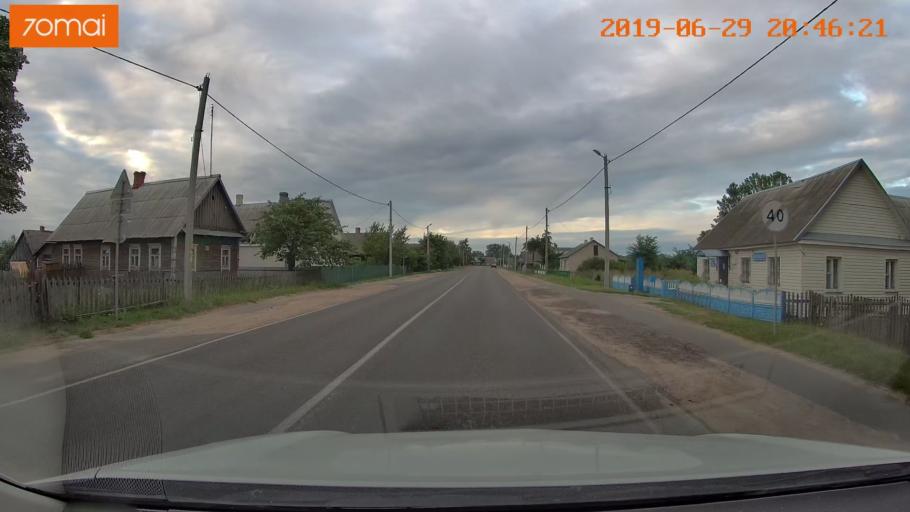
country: BY
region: Brest
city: Hantsavichy
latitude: 52.6303
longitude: 26.3081
